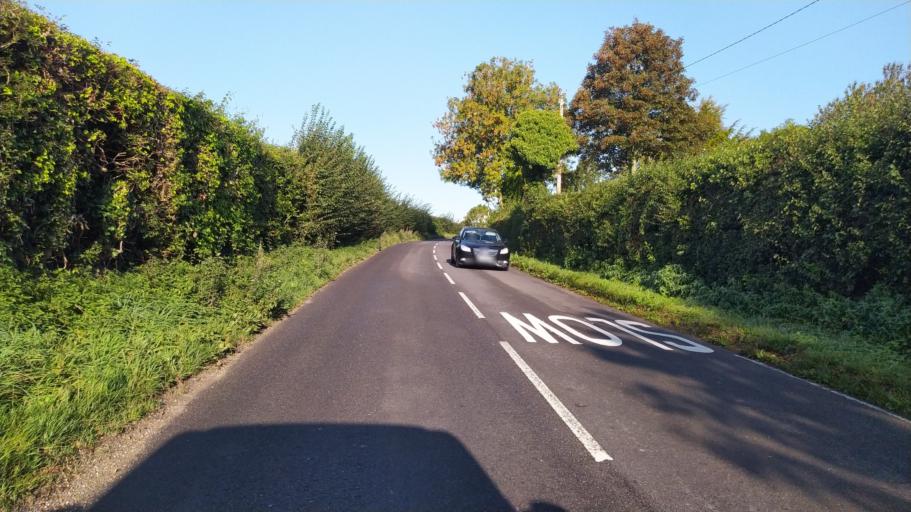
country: GB
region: England
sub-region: Dorset
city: Three Legged Cross
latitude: 50.8675
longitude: -1.9598
